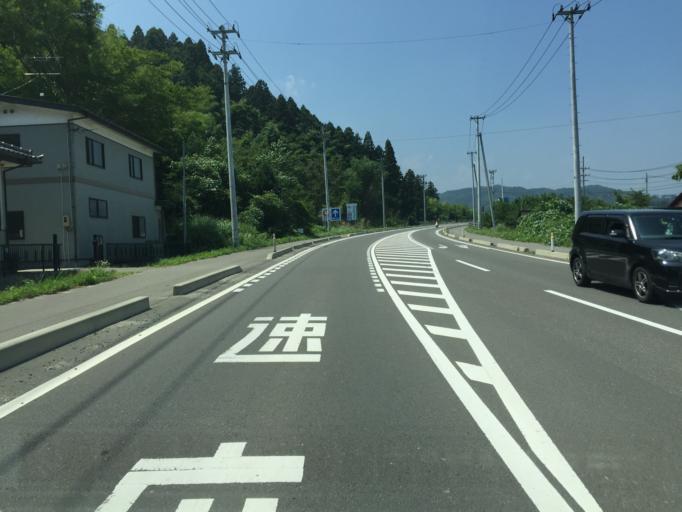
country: JP
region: Miyagi
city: Marumori
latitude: 37.9116
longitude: 140.7769
